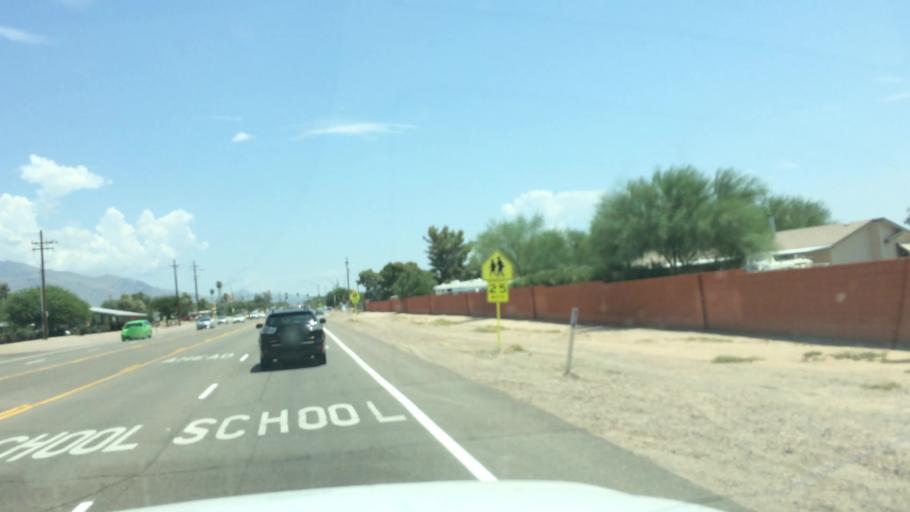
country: US
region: Arizona
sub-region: Pima County
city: Flowing Wells
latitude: 32.3232
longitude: -111.0402
